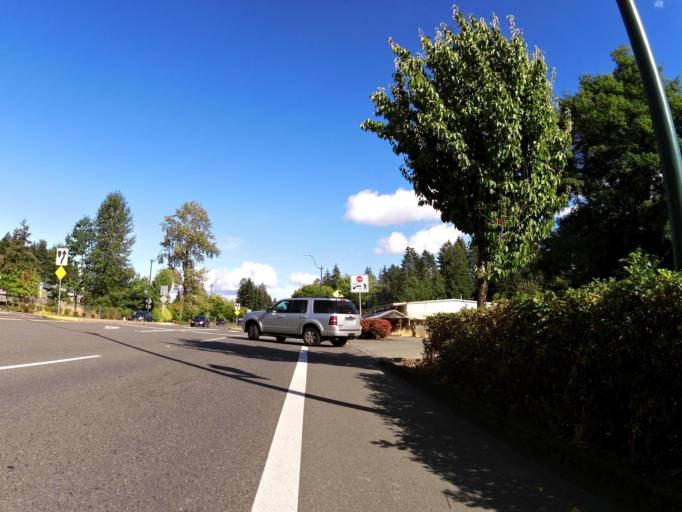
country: US
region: Washington
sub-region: Thurston County
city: Olympia
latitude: 47.0470
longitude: -122.9580
